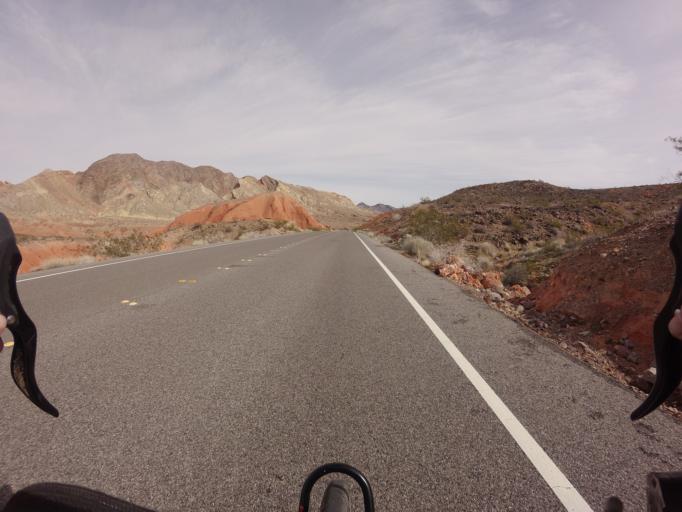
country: US
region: Nevada
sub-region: Clark County
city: Boulder City
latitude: 36.1933
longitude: -114.7290
